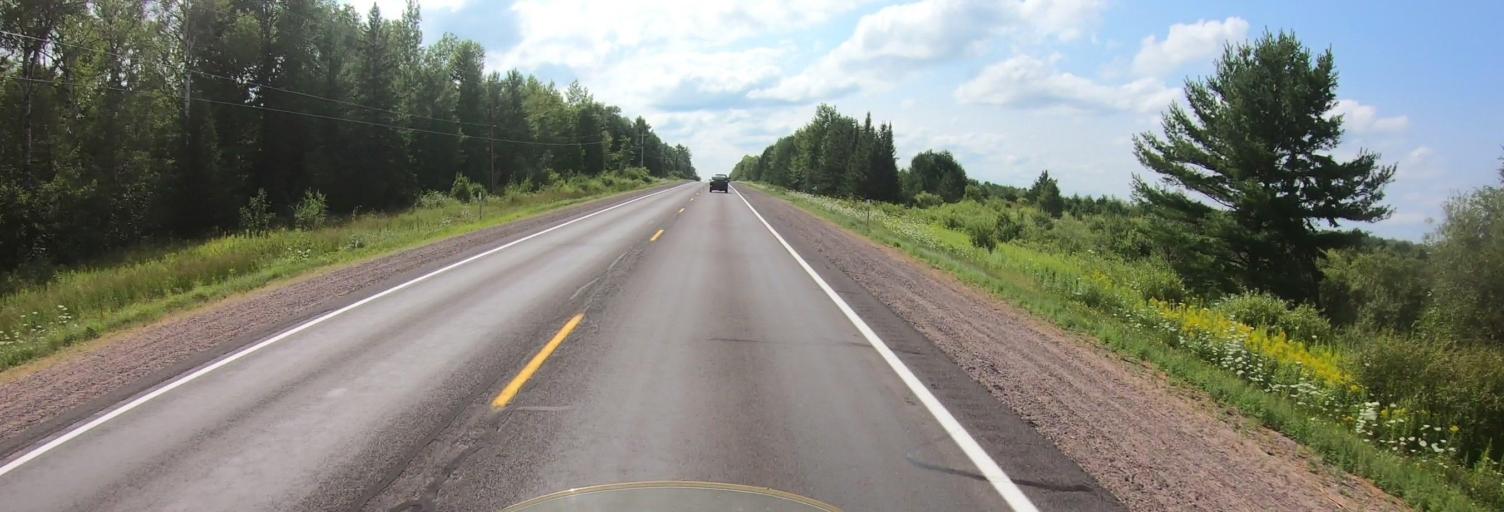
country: US
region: Michigan
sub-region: Ontonagon County
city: Ontonagon
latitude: 46.5348
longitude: -89.2464
